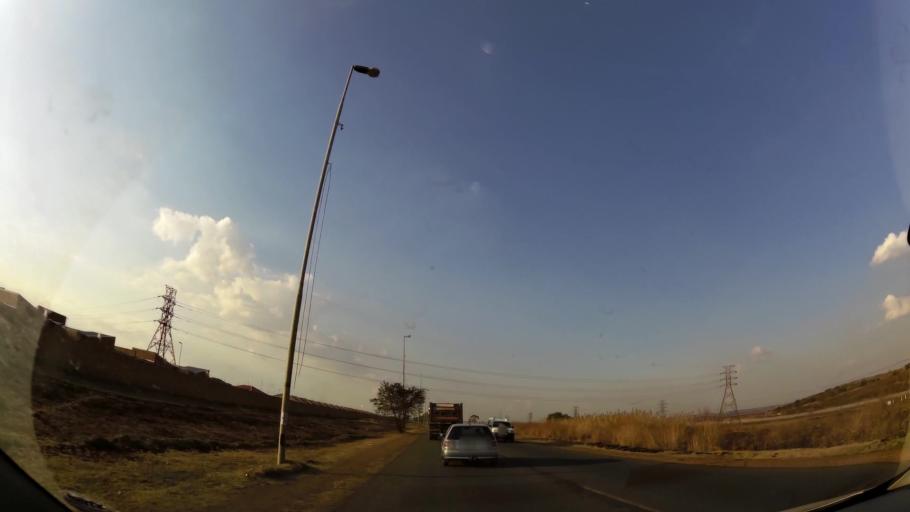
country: ZA
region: Gauteng
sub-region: Ekurhuleni Metropolitan Municipality
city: Boksburg
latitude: -26.3059
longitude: 28.2629
